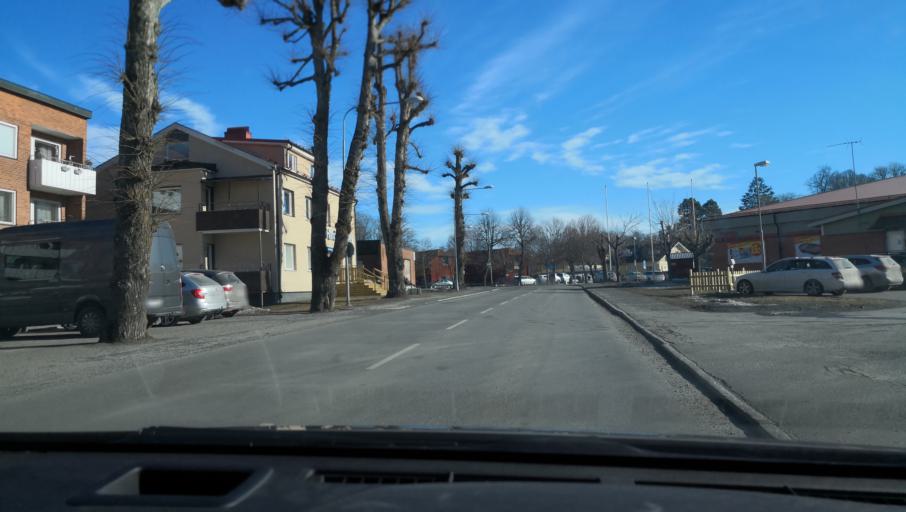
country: SE
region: Uppsala
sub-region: Osthammars Kommun
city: Osterbybruk
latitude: 60.1964
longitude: 17.8946
